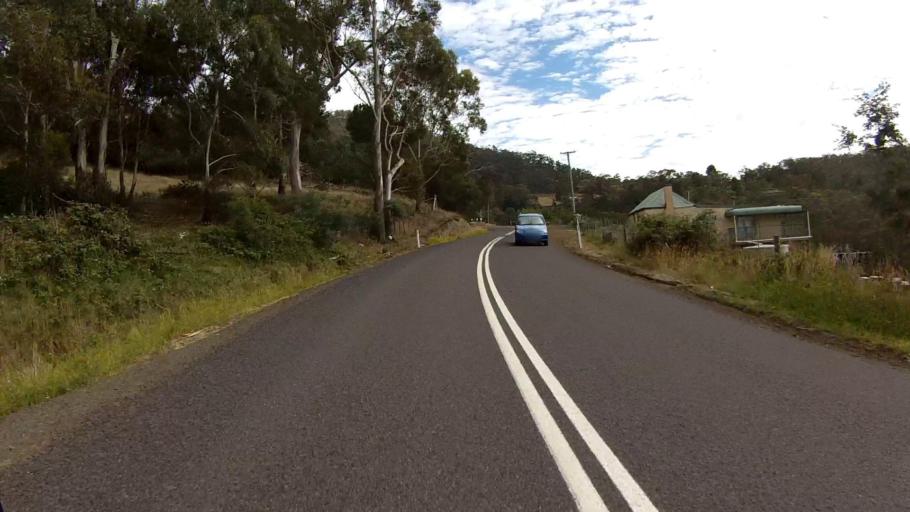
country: AU
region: Tasmania
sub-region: Clarence
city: Lindisfarne
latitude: -42.7872
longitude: 147.3597
